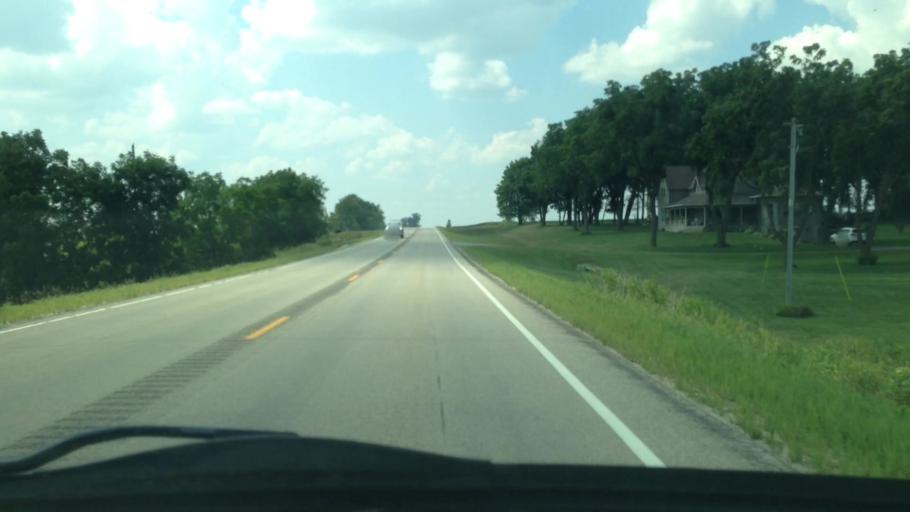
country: US
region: Minnesota
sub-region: Olmsted County
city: Stewartville
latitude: 43.8555
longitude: -92.4159
